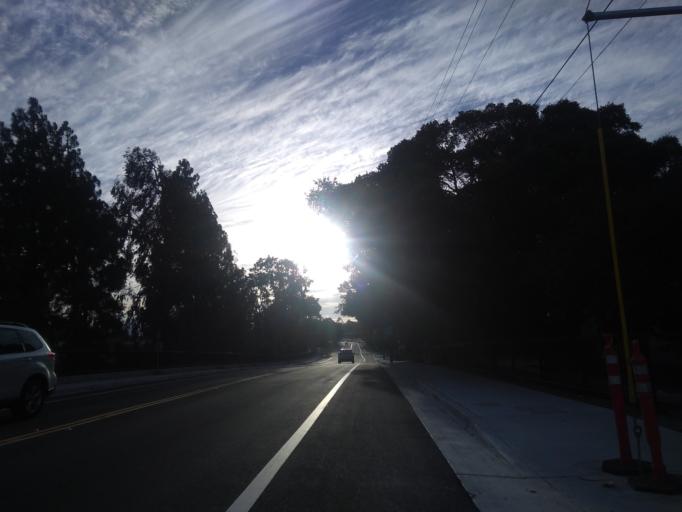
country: US
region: California
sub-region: Santa Clara County
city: Sunnyvale
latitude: 37.4108
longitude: -121.9869
